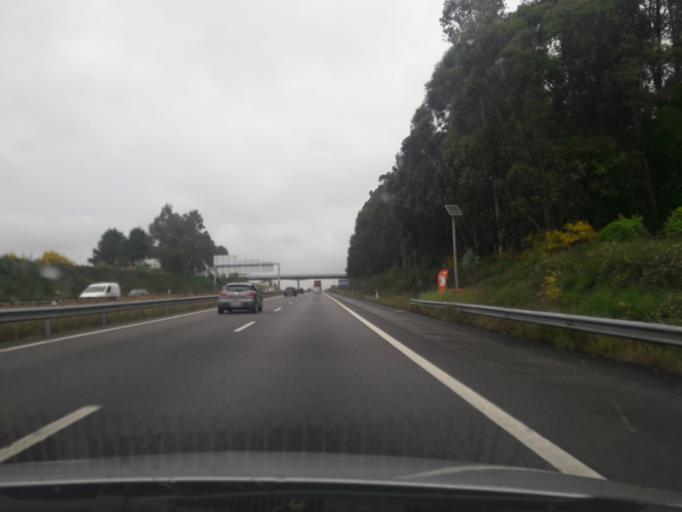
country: PT
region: Porto
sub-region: Vila do Conde
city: Arvore
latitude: 41.3379
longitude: -8.7122
